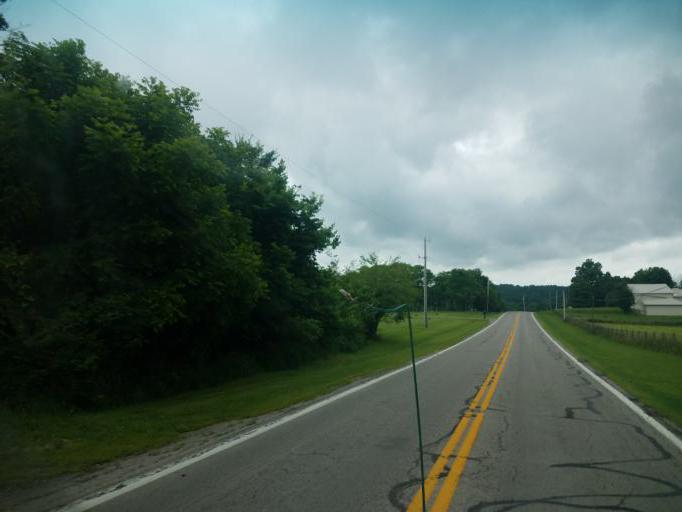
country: US
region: Ohio
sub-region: Logan County
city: Bellefontaine
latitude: 40.3750
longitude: -83.6611
